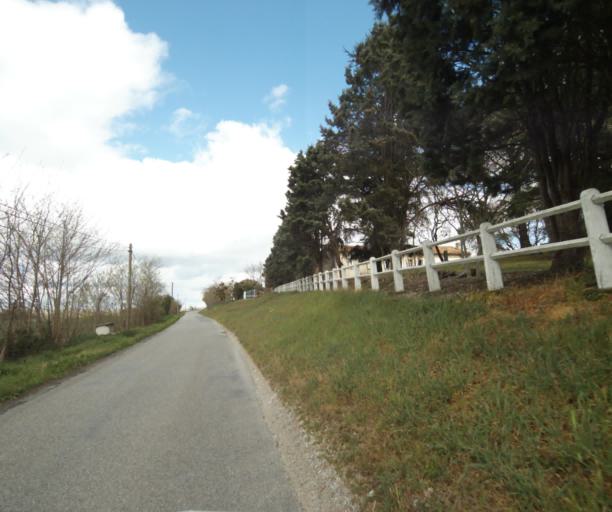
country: FR
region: Midi-Pyrenees
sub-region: Departement de l'Ariege
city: Saverdun
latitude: 43.2452
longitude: 1.5891
